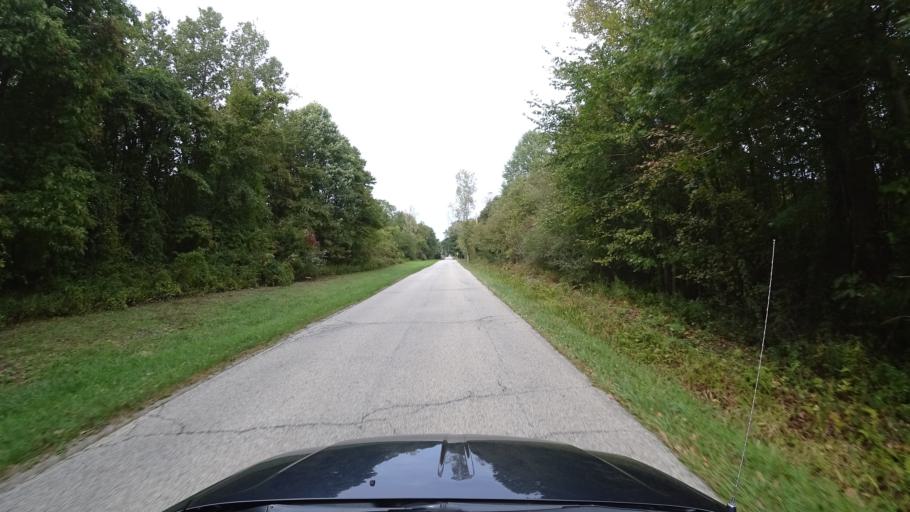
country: US
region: Indiana
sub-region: LaPorte County
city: Long Beach
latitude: 41.7346
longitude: -86.8162
